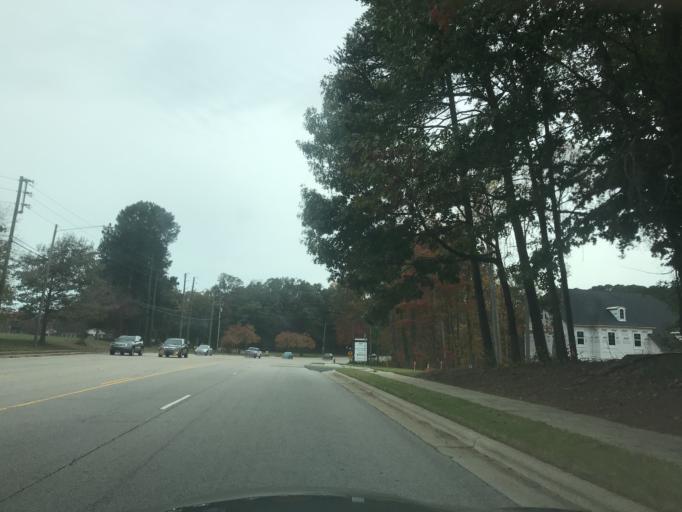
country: US
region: North Carolina
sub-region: Wake County
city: West Raleigh
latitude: 35.8575
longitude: -78.6686
